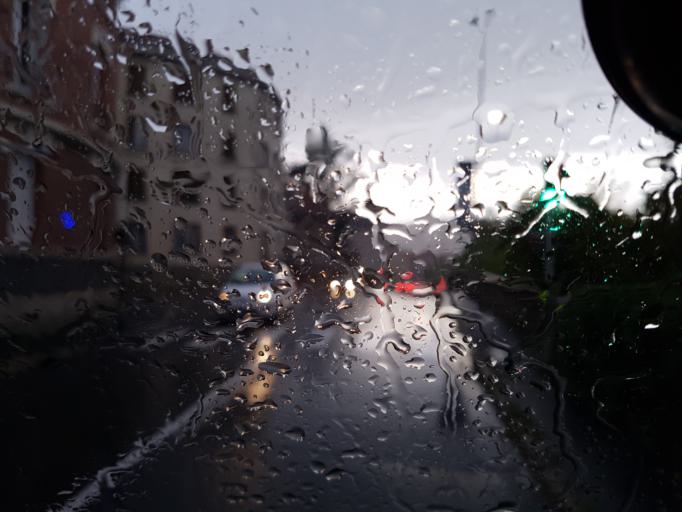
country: FR
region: Auvergne
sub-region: Departement de la Haute-Loire
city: Le Puy-en-Velay
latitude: 45.0417
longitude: 3.8920
